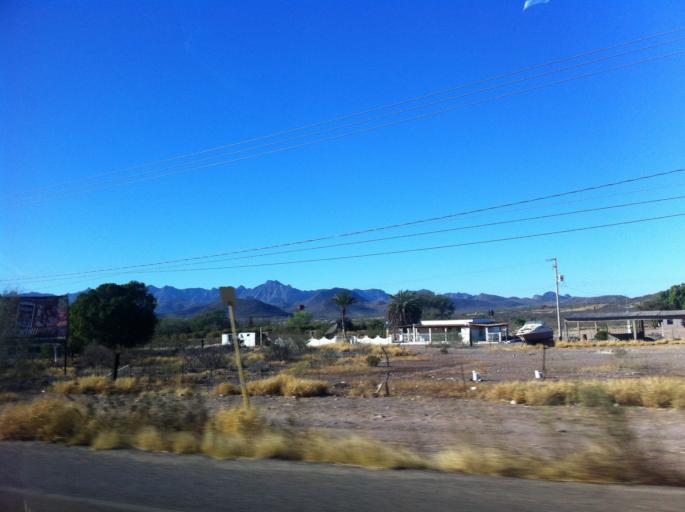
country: MX
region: Sonora
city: Heroica Guaymas
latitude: 27.9837
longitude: -110.9545
